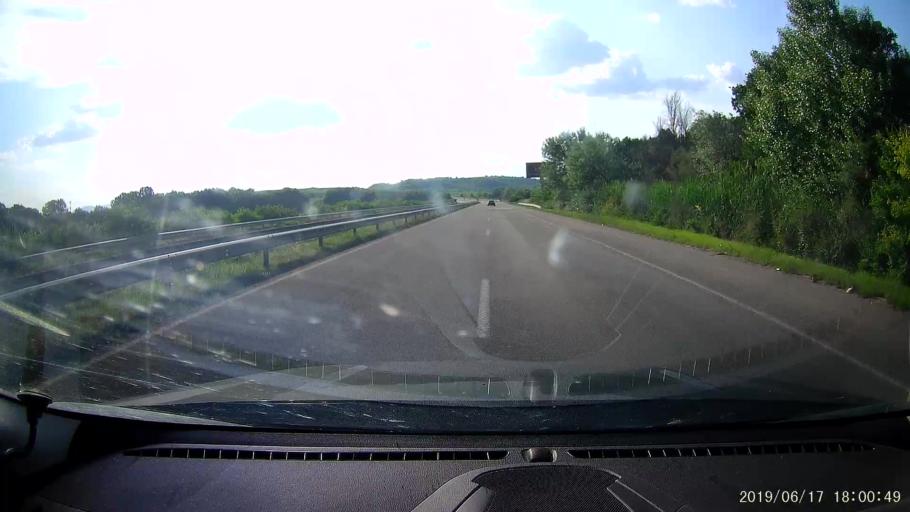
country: BG
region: Khaskovo
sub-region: Obshtina Svilengrad
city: Svilengrad
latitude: 41.7409
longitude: 26.2710
